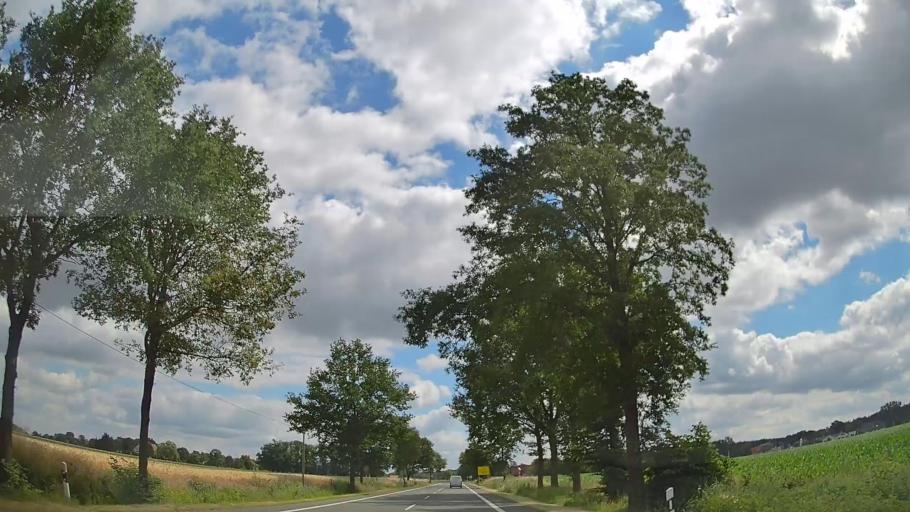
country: DE
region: North Rhine-Westphalia
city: Espelkamp
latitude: 52.3918
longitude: 8.5474
